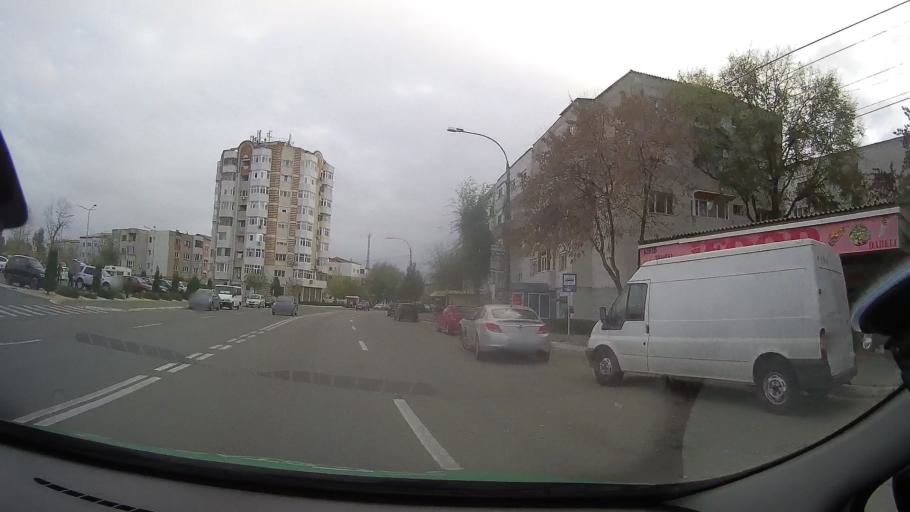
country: RO
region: Constanta
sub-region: Municipiul Medgidia
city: Medgidia
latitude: 44.2620
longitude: 28.2621
